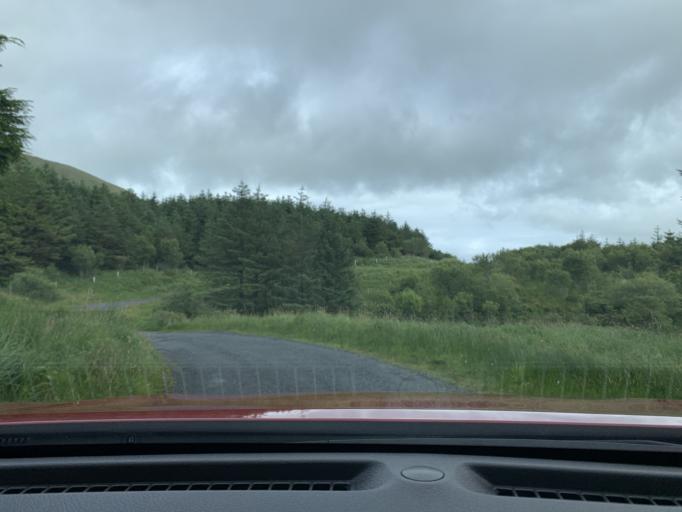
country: IE
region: Connaught
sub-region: Sligo
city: Sligo
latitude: 54.3800
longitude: -8.4128
